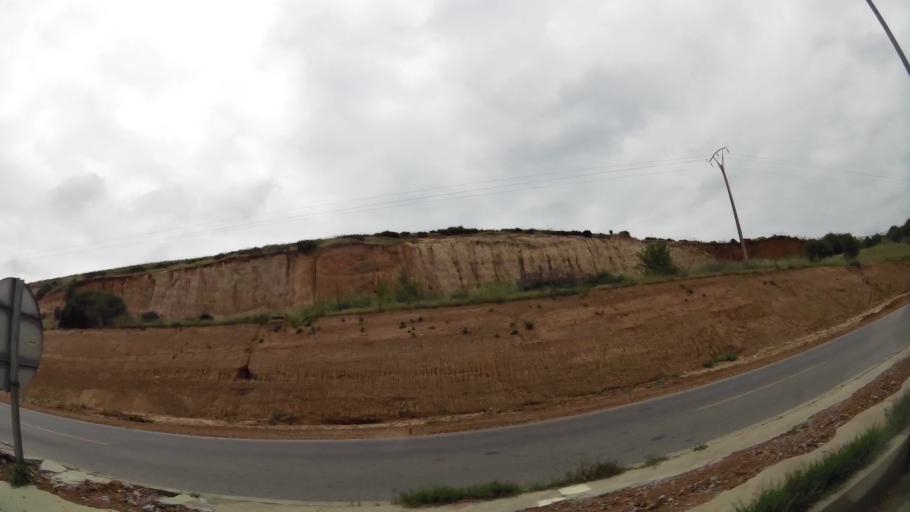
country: MA
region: Rabat-Sale-Zemmour-Zaer
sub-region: Rabat
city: Rabat
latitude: 33.9813
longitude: -6.8030
